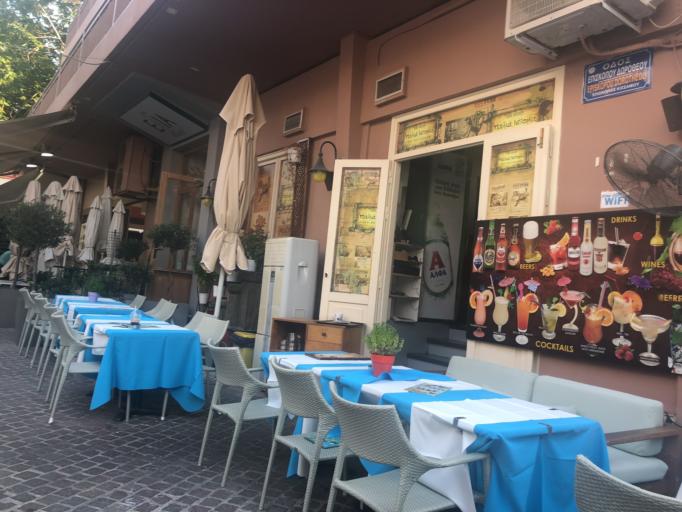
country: GR
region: Crete
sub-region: Nomos Chanias
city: Chania
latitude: 35.5151
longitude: 24.0188
